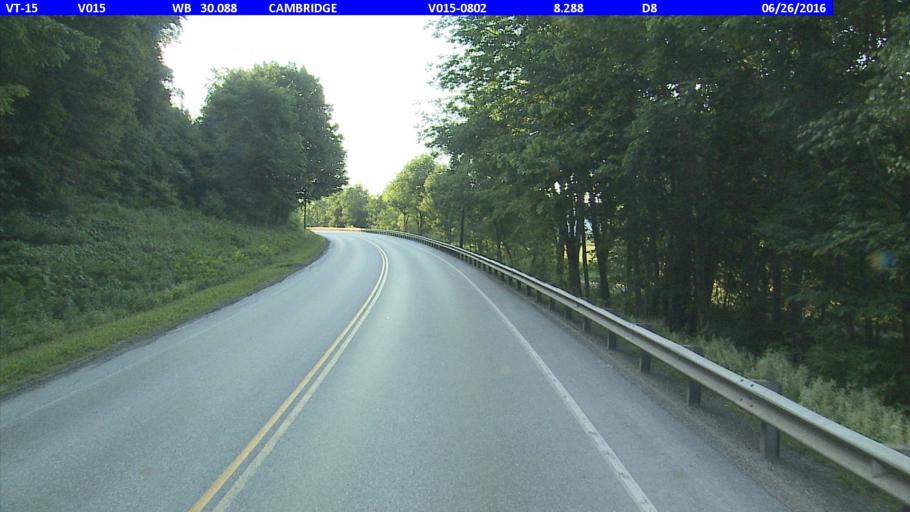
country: US
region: Vermont
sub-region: Lamoille County
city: Johnson
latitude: 44.6652
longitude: -72.7757
